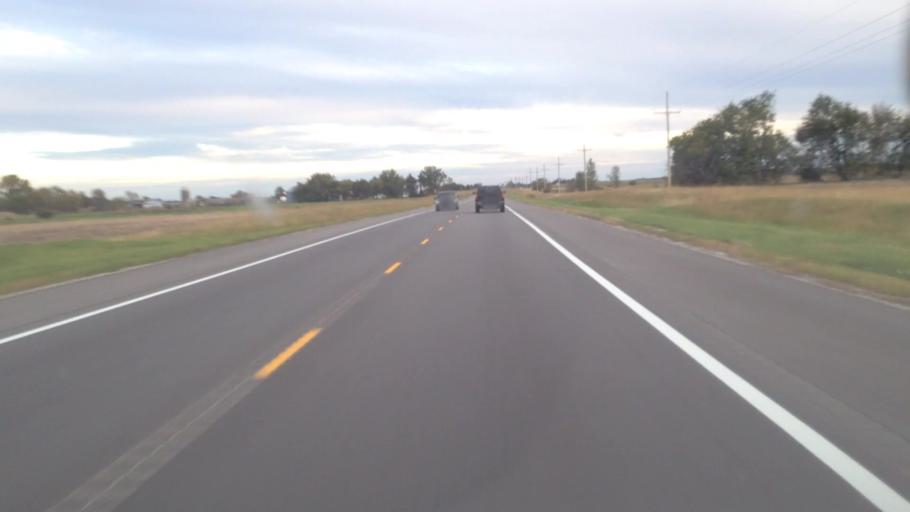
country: US
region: Kansas
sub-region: Franklin County
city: Ottawa
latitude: 38.5295
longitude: -95.2677
